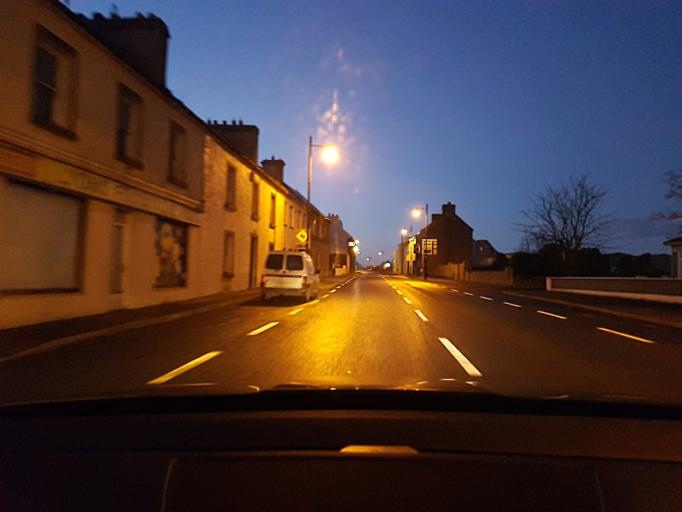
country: IE
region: Connaught
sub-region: Maigh Eo
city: Ballinrobe
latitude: 53.5801
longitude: -9.1221
